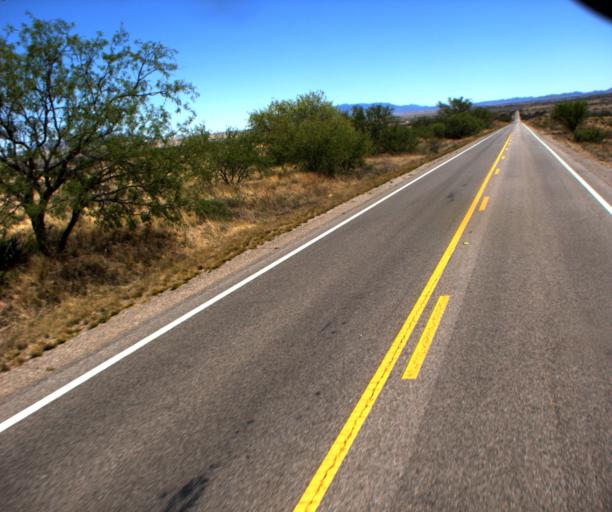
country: US
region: Arizona
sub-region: Pima County
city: Corona de Tucson
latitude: 31.7643
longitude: -110.6800
